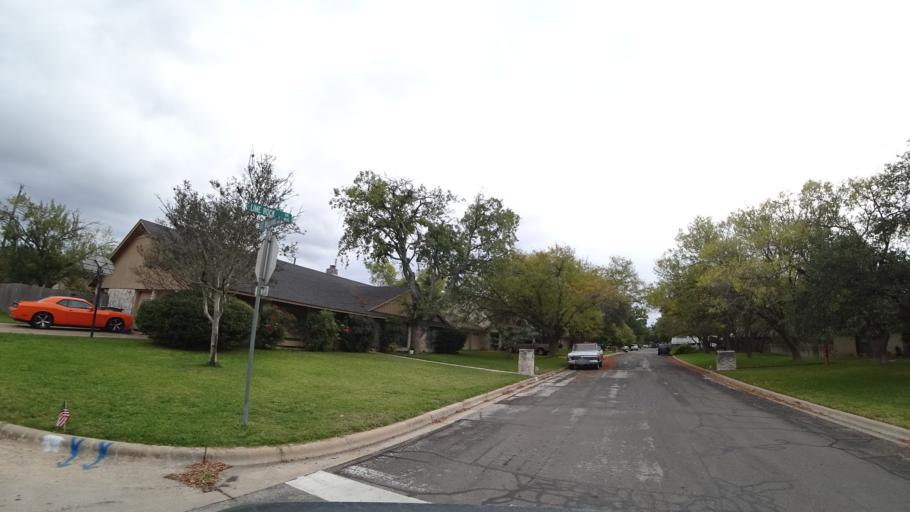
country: US
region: Texas
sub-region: Williamson County
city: Round Rock
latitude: 30.5000
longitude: -97.6927
